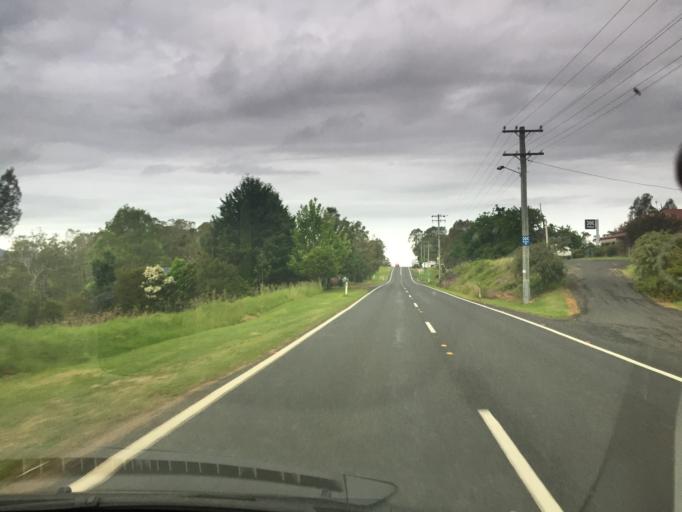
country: AU
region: New South Wales
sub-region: Bega Valley
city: Bega
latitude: -36.6295
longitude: 149.5725
